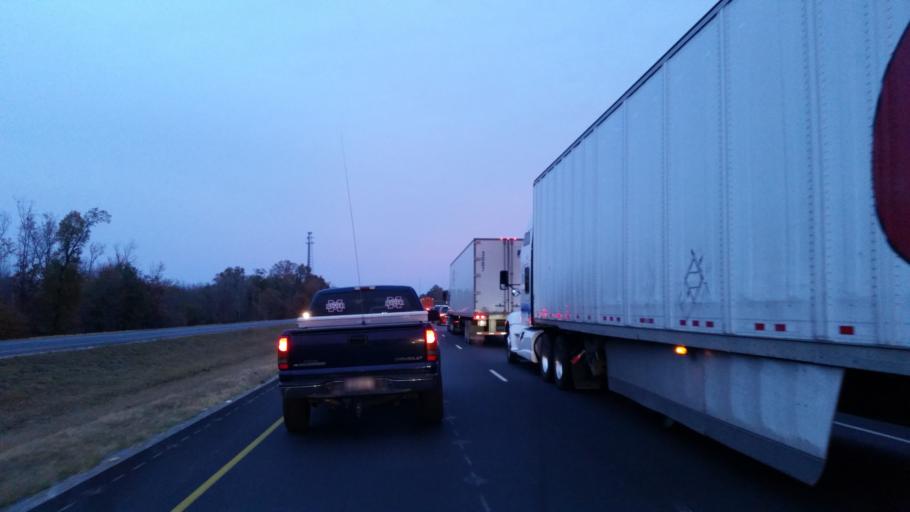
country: US
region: Alabama
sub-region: Tuscaloosa County
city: Tuscaloosa
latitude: 33.1542
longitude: -87.5932
